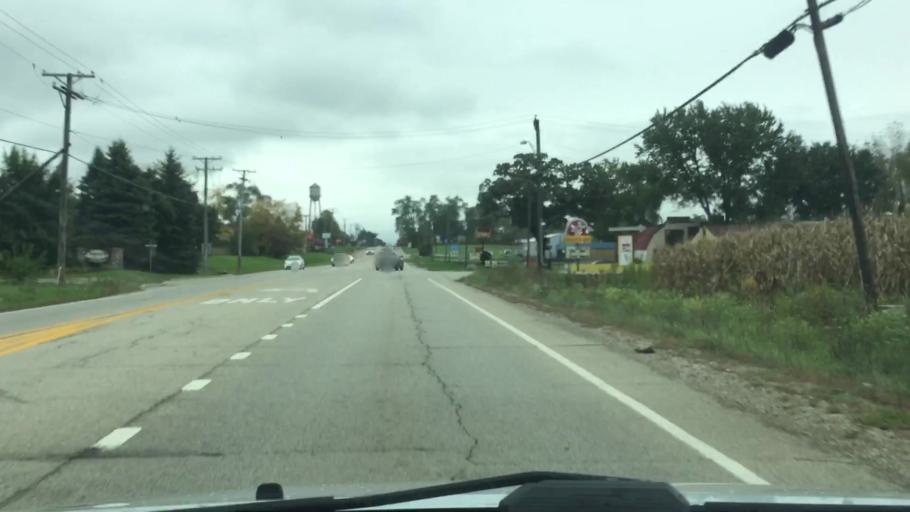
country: US
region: Illinois
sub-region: McHenry County
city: Richmond
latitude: 42.4873
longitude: -88.3062
